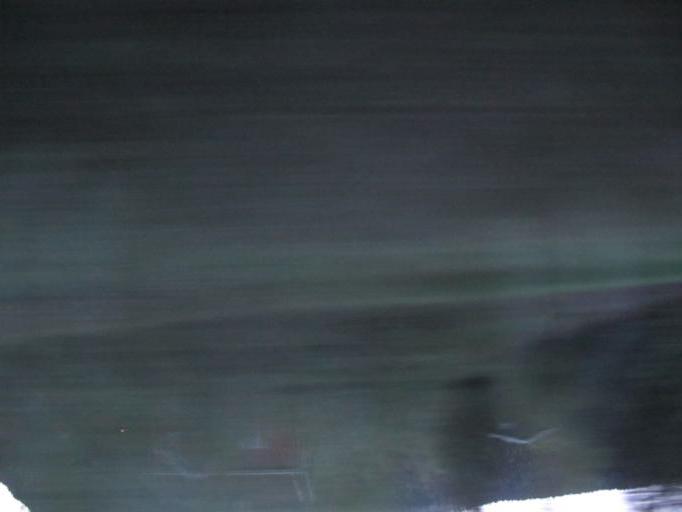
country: NO
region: Oppland
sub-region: Sor-Fron
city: Hundorp
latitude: 61.5747
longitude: 9.8588
